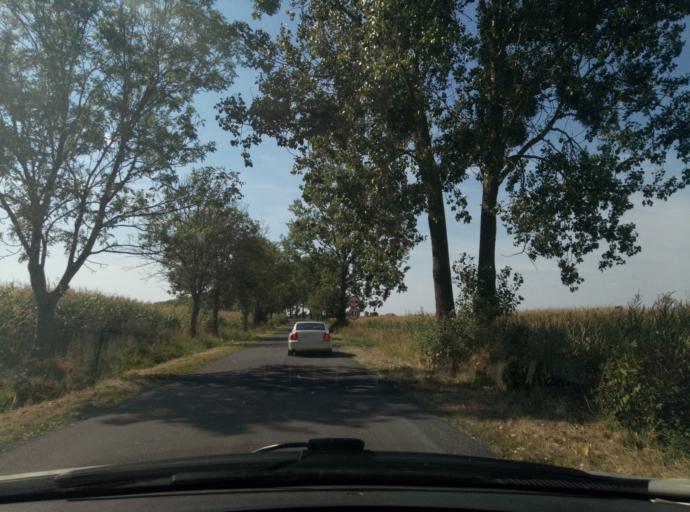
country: PL
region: Kujawsko-Pomorskie
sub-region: Powiat brodnicki
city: Jablonowo Pomorskie
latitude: 53.4003
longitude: 19.2204
